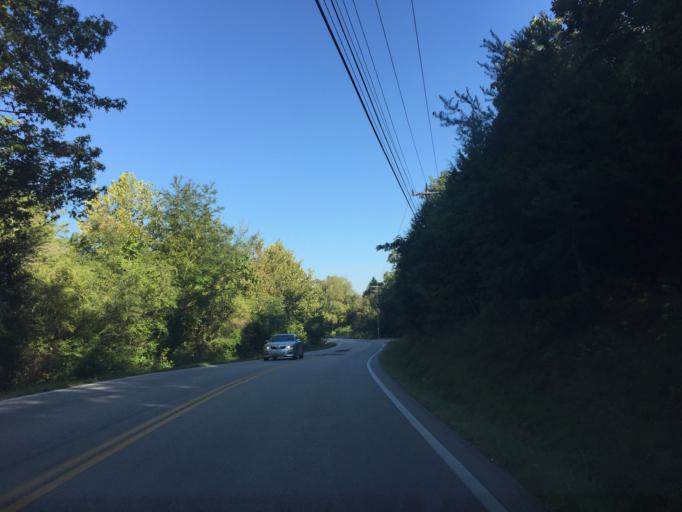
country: US
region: Tennessee
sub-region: Hamilton County
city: Harrison
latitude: 35.1186
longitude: -85.0833
